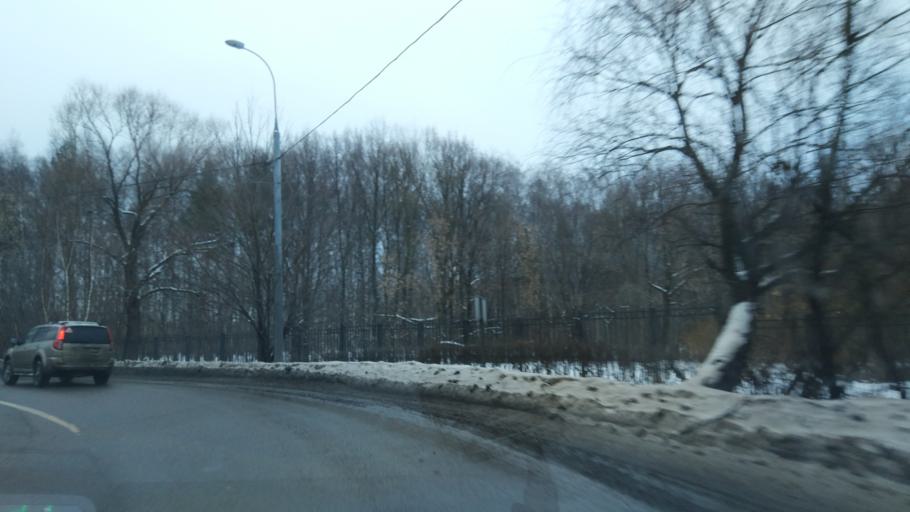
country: RU
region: Moskovskaya
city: Izmaylovo
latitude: 55.7890
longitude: 37.8232
